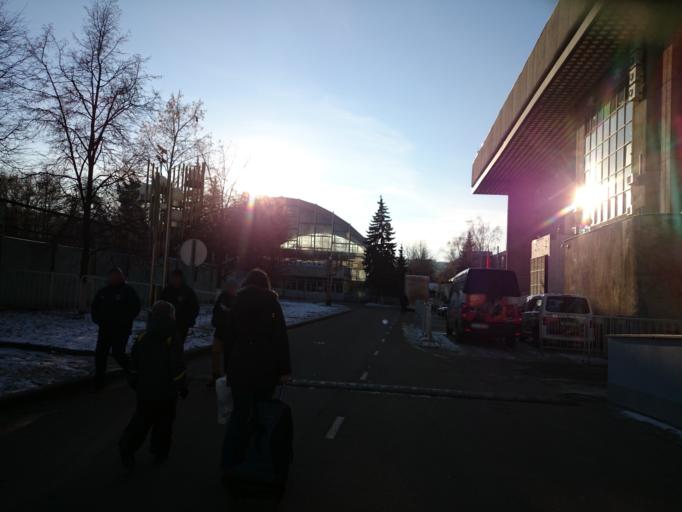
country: RU
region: Moscow
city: Sokol
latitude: 55.7946
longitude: 37.5388
